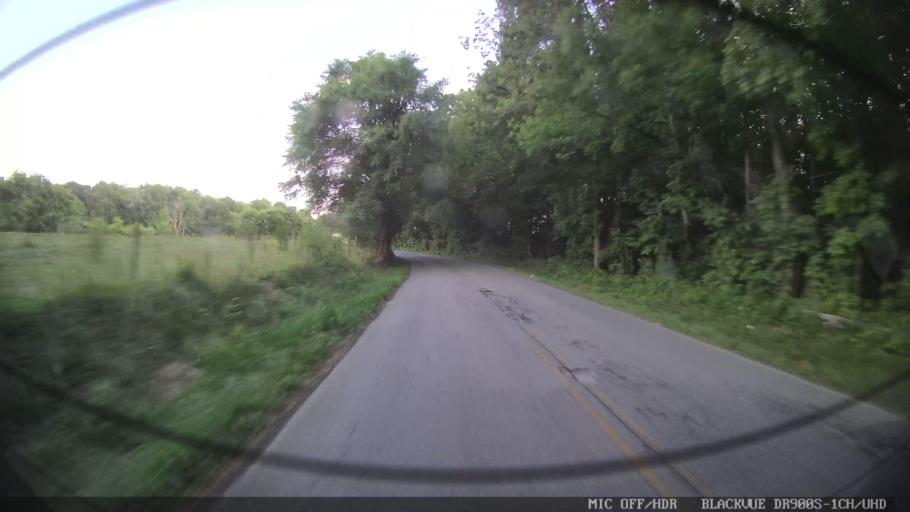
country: US
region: Georgia
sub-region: Bartow County
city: Rydal
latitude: 34.2739
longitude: -84.7989
